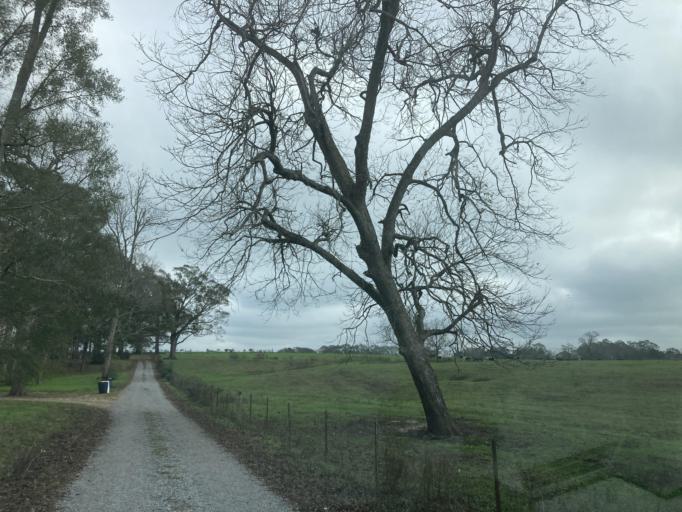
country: US
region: Mississippi
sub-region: Stone County
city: Wiggins
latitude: 30.8987
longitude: -89.1617
